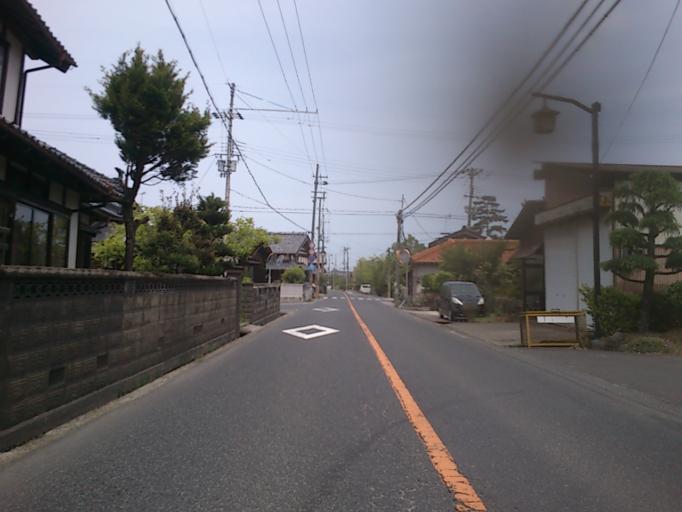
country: JP
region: Kyoto
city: Miyazu
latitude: 35.5889
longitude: 135.1015
